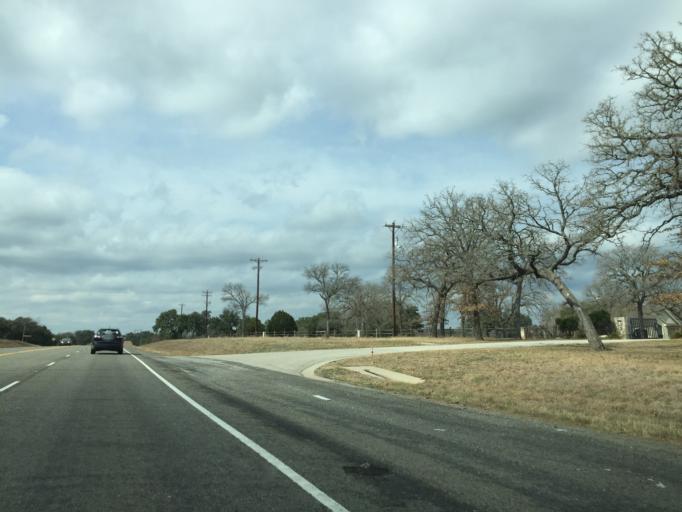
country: US
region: Texas
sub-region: Burnet County
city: Meadowlakes
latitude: 30.4933
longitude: -98.2413
